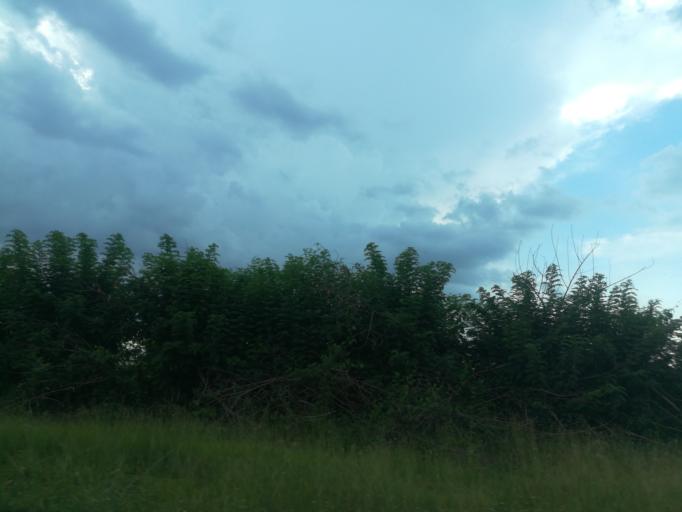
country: NG
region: Oyo
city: Ibadan
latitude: 7.4314
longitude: 3.8928
